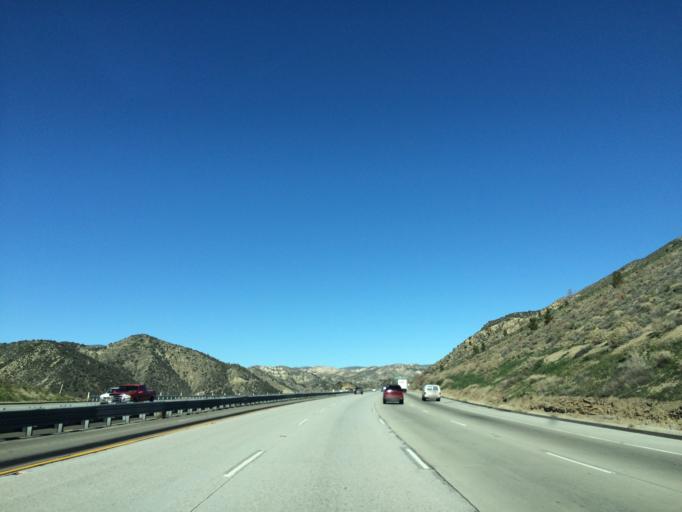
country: US
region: California
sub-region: Kern County
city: Lebec
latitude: 34.6887
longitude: -118.7869
